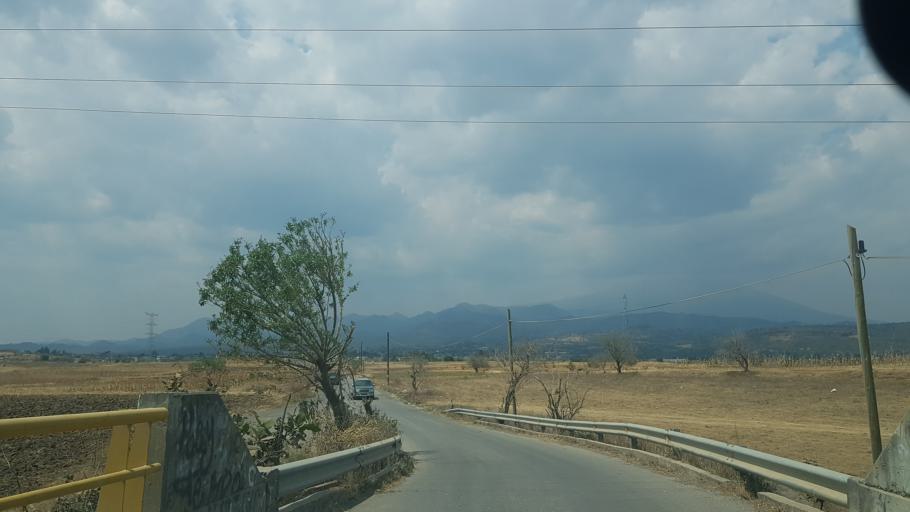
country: MX
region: Puebla
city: San Juan Amecac
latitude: 18.8174
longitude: -98.6521
